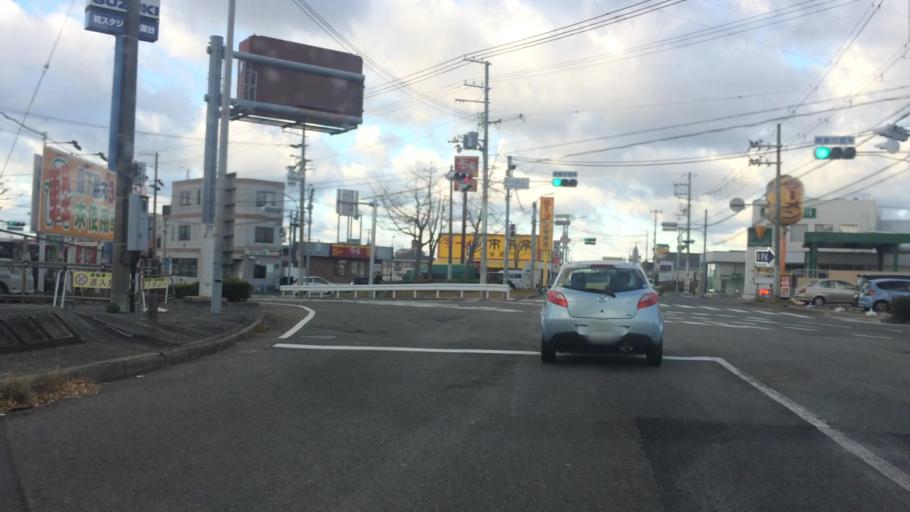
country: JP
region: Hyogo
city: Akashi
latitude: 34.6622
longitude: 135.0241
